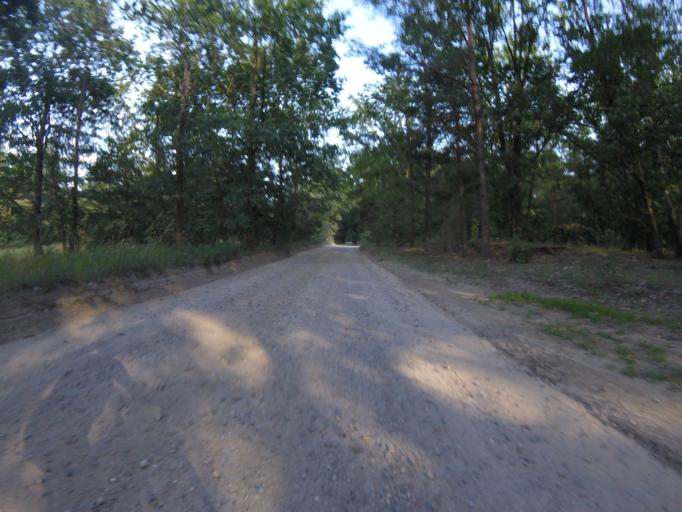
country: DE
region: Brandenburg
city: Zossen
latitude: 52.2077
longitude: 13.4868
